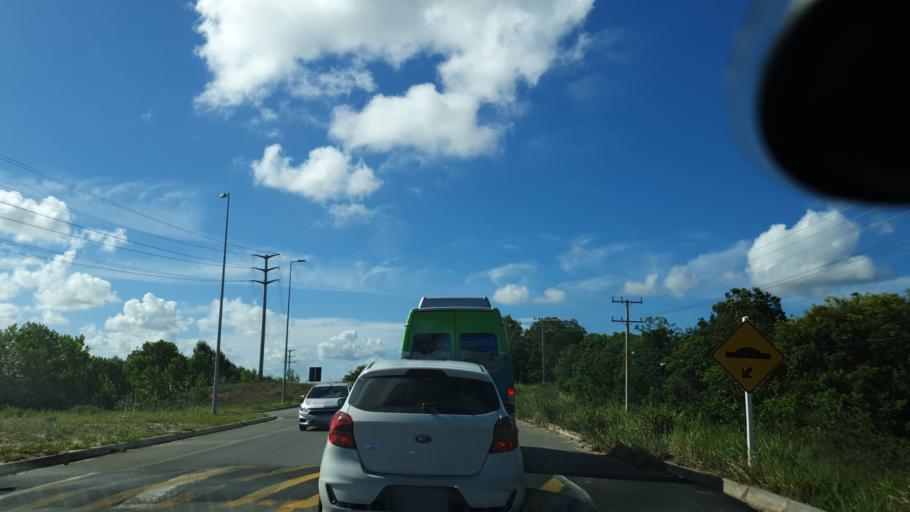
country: BR
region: Bahia
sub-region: Camacari
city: Camacari
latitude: -12.6919
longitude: -38.2249
